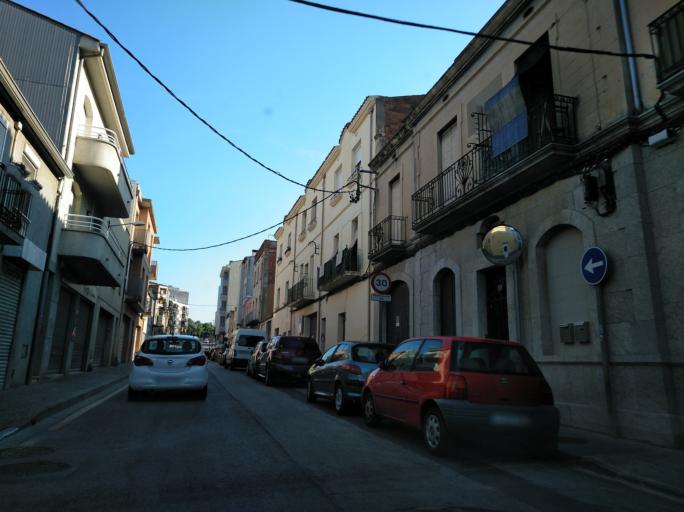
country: ES
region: Catalonia
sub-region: Provincia de Girona
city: Girona
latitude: 41.9694
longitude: 2.8215
